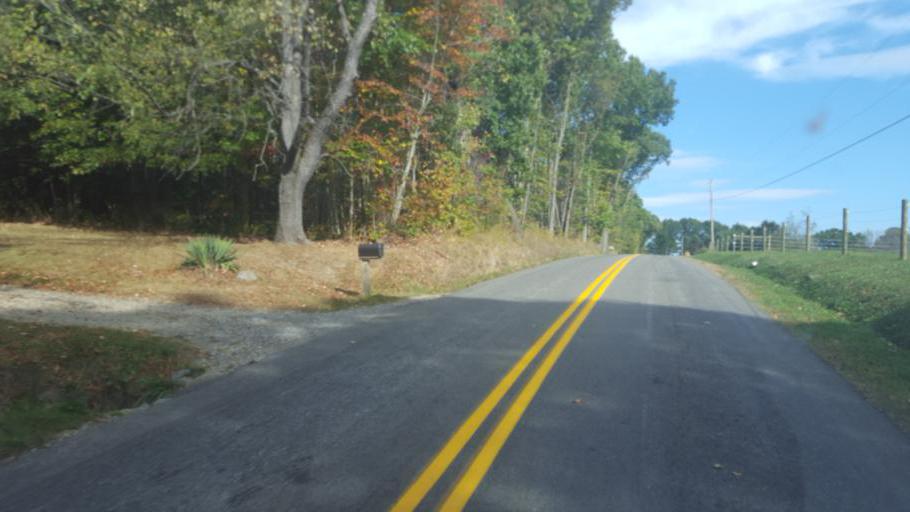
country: US
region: Pennsylvania
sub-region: Mercer County
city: Mercer
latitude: 41.3489
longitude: -80.2538
